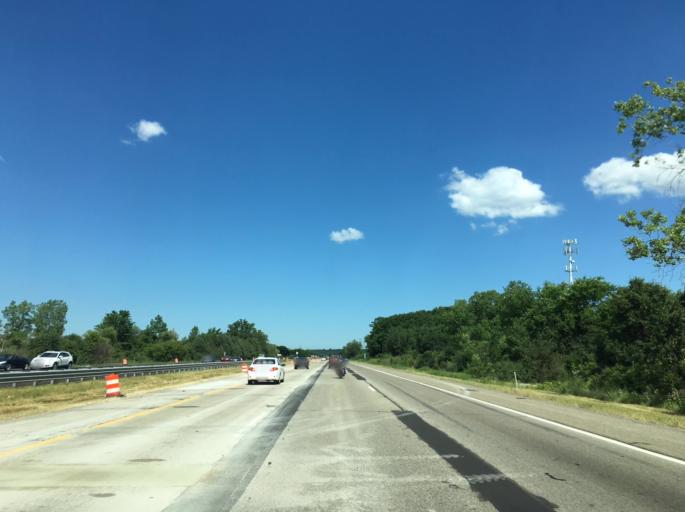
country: US
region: Michigan
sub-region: Oakland County
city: Waterford
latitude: 42.7138
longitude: -83.3390
